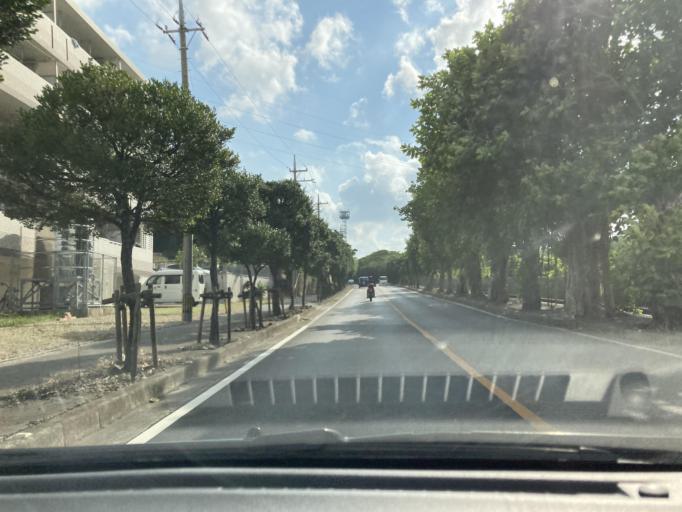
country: JP
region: Okinawa
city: Tomigusuku
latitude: 26.1638
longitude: 127.7330
